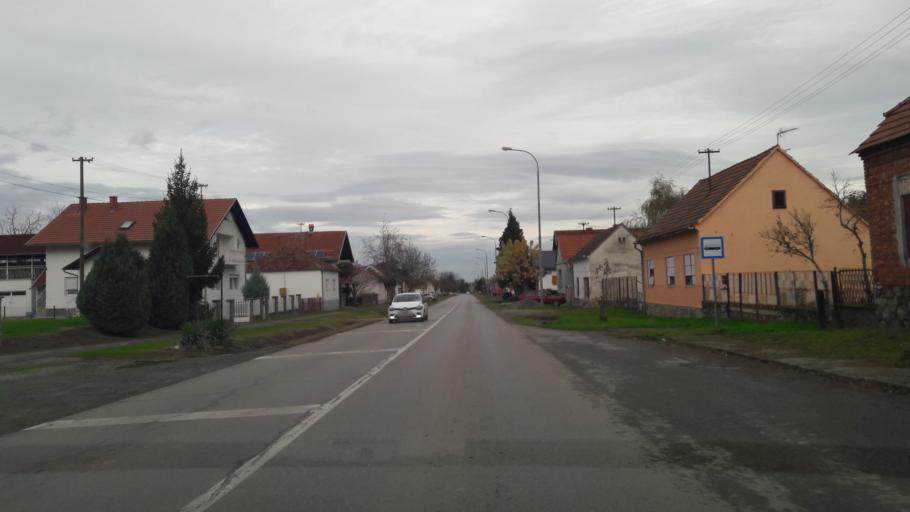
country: HR
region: Virovitick-Podravska
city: Orahovica
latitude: 45.5393
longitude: 17.8948
